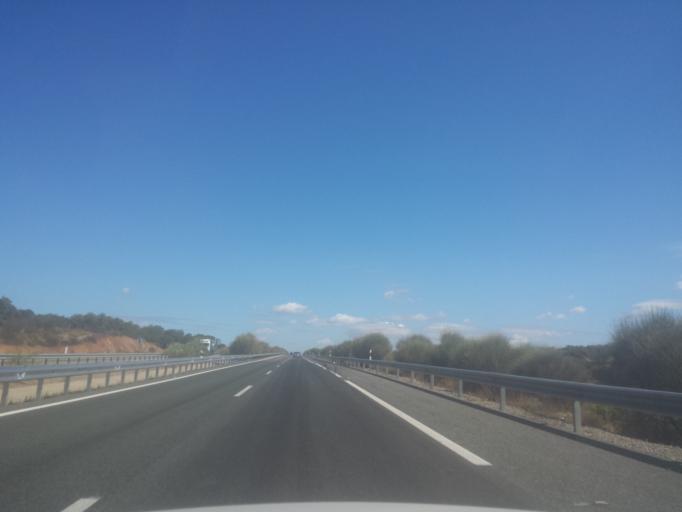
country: ES
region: Andalusia
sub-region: Provincia de Huelva
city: Santa Olalla del Cala
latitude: 37.8644
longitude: -6.2185
